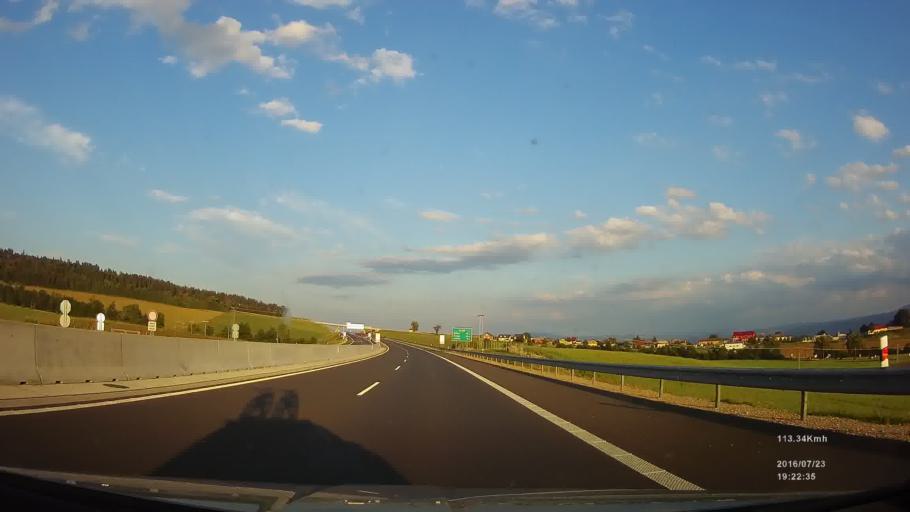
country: SK
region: Presovsky
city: Lubica
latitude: 49.0090
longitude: 20.4616
